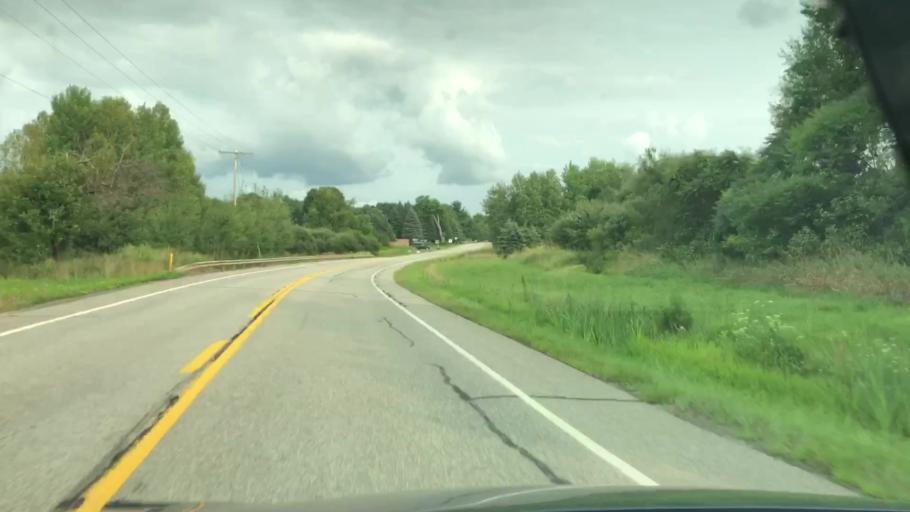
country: US
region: Pennsylvania
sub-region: Erie County
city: Union City
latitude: 42.0570
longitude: -79.8574
